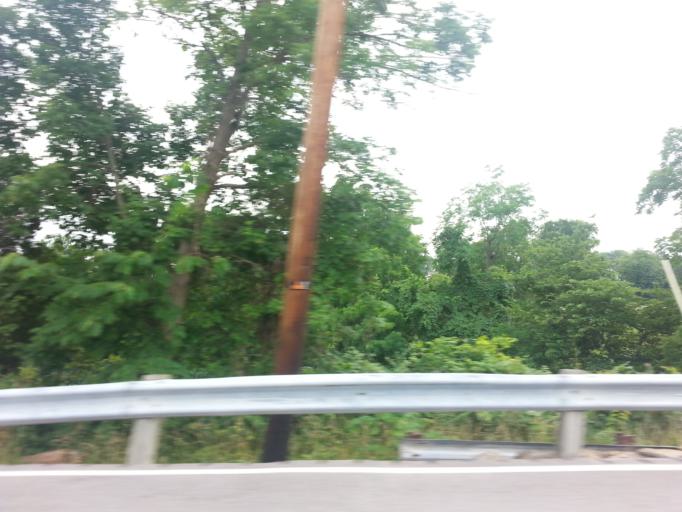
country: US
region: Kentucky
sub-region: Robertson County
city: Mount Olivet
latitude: 38.5334
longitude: -84.0207
